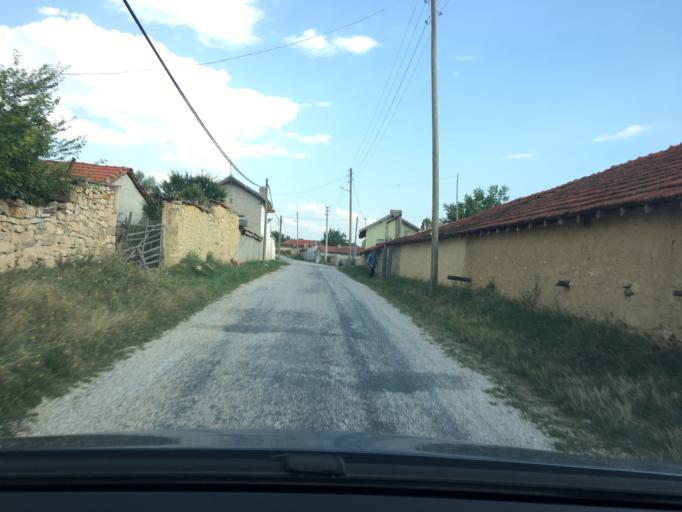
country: TR
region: Eskisehir
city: Kirka
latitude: 39.2784
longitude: 30.6750
